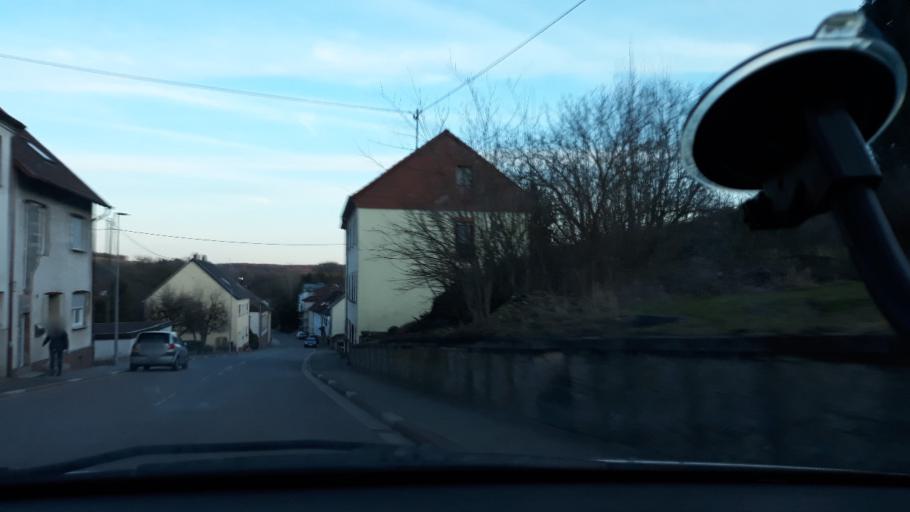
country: DE
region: Saarland
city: Sankt Ingbert
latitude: 49.2275
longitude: 7.1391
